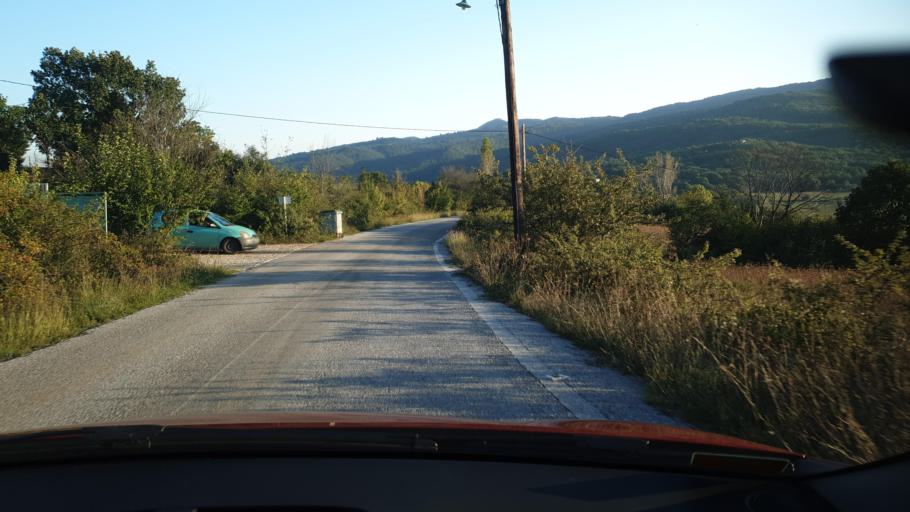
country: GR
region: Central Macedonia
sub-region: Nomos Chalkidikis
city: Galatista
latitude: 40.5284
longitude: 23.2776
